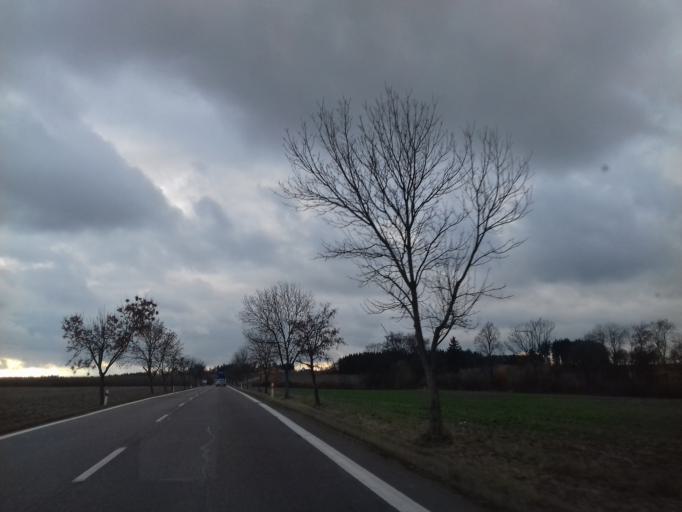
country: CZ
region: Pardubicky
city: Radimer
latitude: 49.7437
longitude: 16.4041
